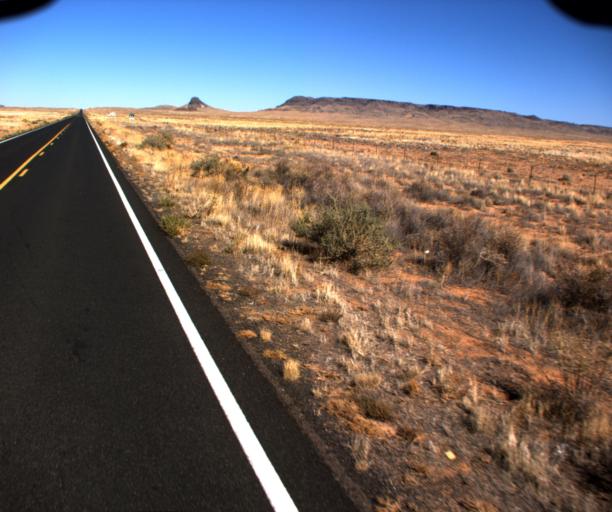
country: US
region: Arizona
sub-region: Navajo County
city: Dilkon
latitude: 35.3714
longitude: -110.4250
